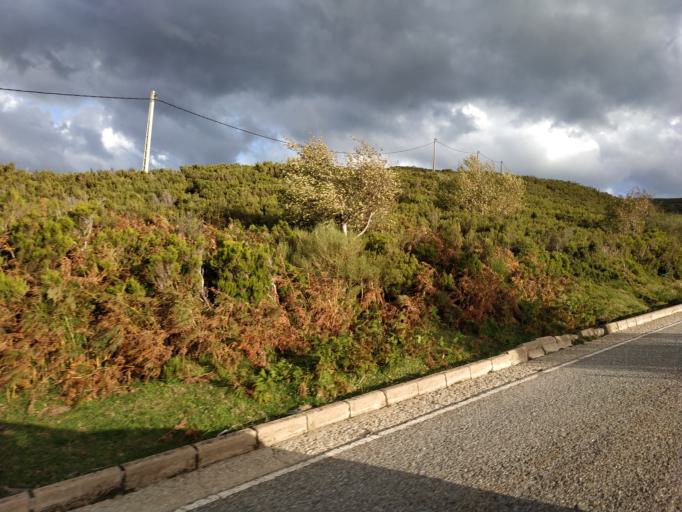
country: ES
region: Castille and Leon
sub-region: Provincia de Leon
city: Candin
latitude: 42.8728
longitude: -6.8226
